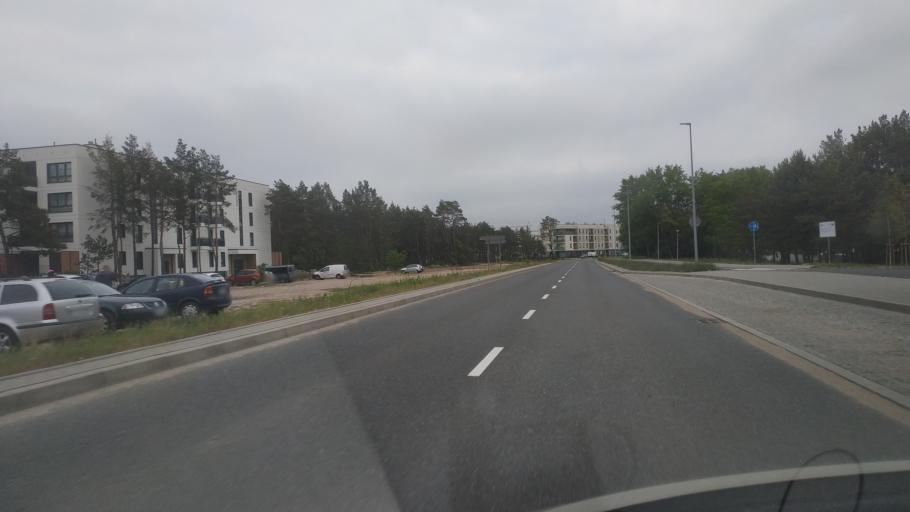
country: PL
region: Kujawsko-Pomorskie
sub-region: Torun
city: Torun
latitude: 53.0503
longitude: 18.6041
